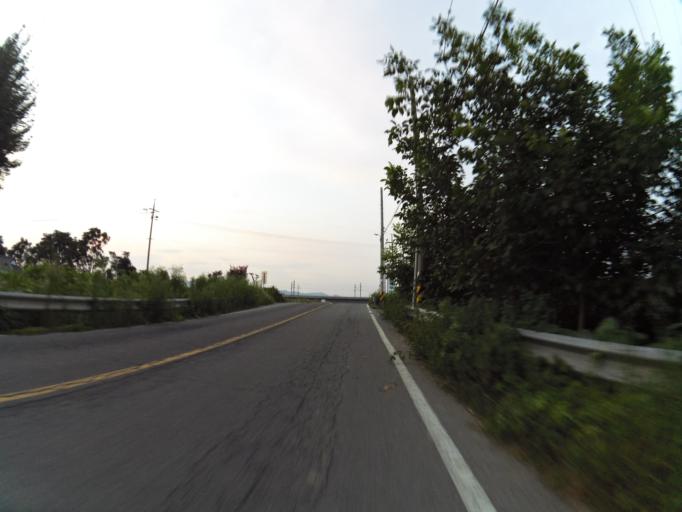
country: KR
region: Gyeongsangbuk-do
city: Gyeongsan-si
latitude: 35.8508
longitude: 128.7473
